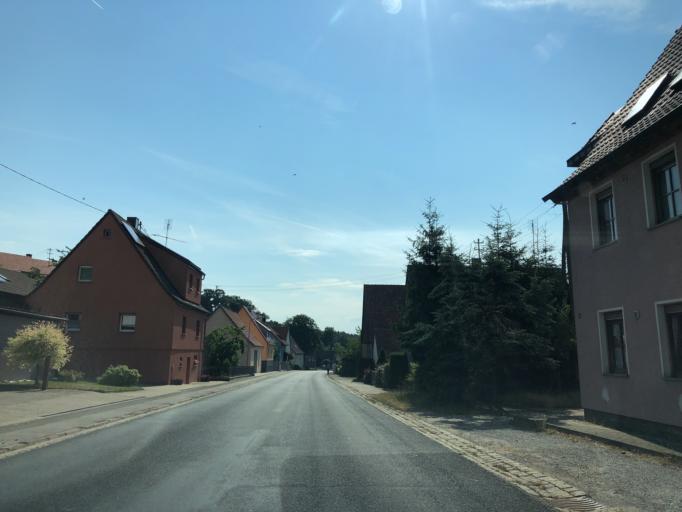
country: DE
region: Bavaria
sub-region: Regierungsbezirk Unterfranken
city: Geiselwind
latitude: 49.7692
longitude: 10.5240
